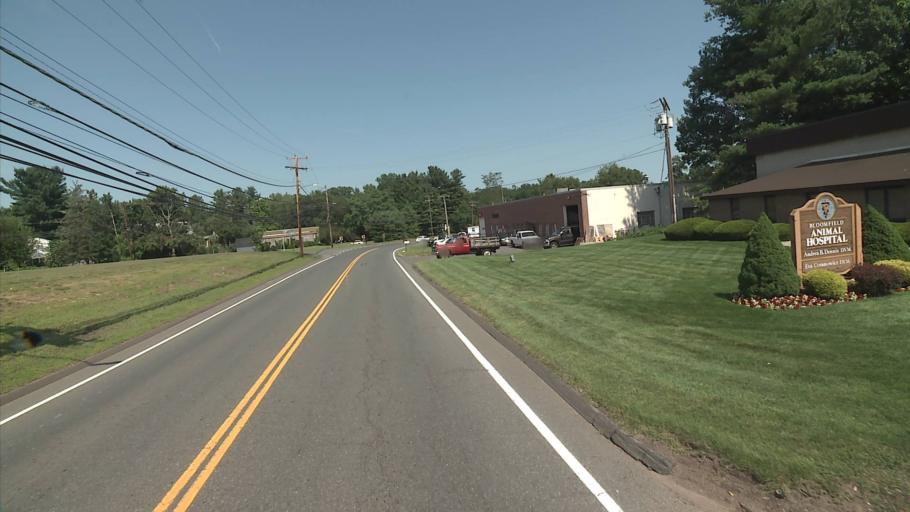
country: US
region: Connecticut
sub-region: Hartford County
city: Blue Hills
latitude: 41.8609
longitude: -72.6947
